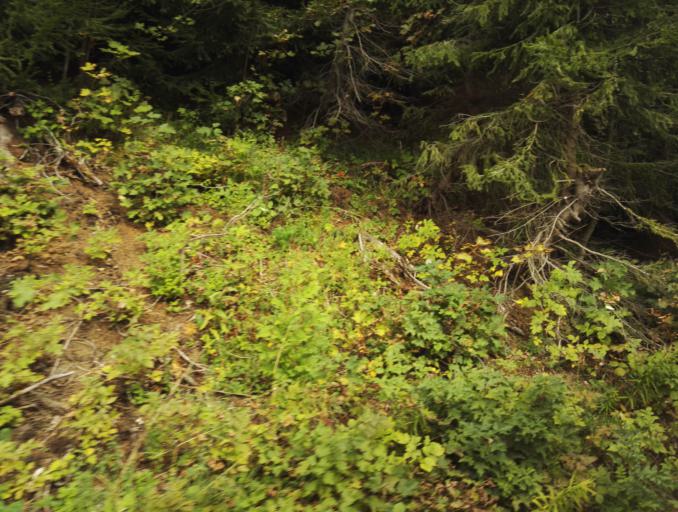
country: AT
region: Styria
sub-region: Politischer Bezirk Leoben
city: Vordernberg
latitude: 47.5133
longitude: 14.9756
